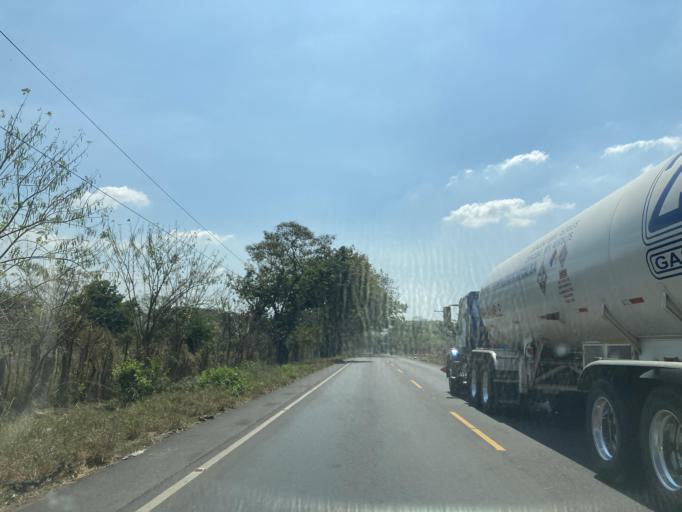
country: GT
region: Escuintla
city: Guanagazapa
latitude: 14.2208
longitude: -90.7286
